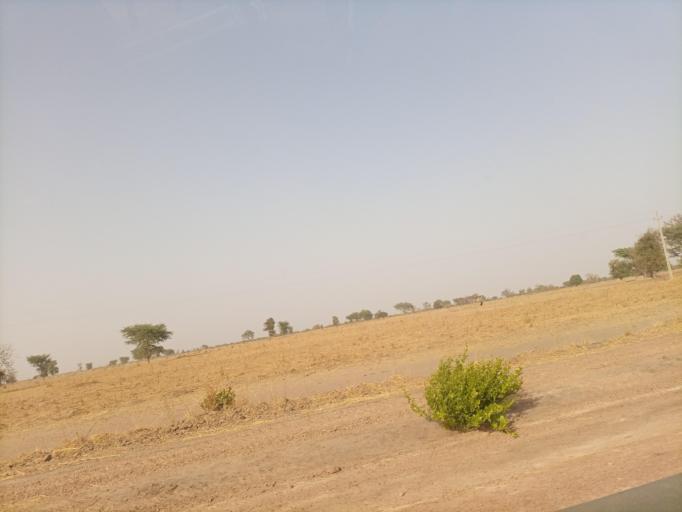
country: SN
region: Fatick
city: Passi
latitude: 14.0284
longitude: -16.3070
